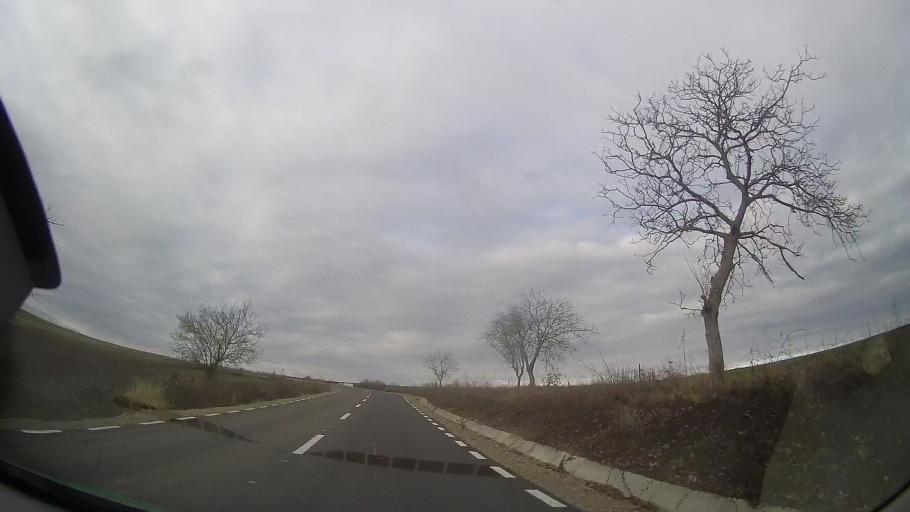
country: RO
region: Bistrita-Nasaud
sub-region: Comuna Teaca
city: Ocnita
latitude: 46.8271
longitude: 24.4755
